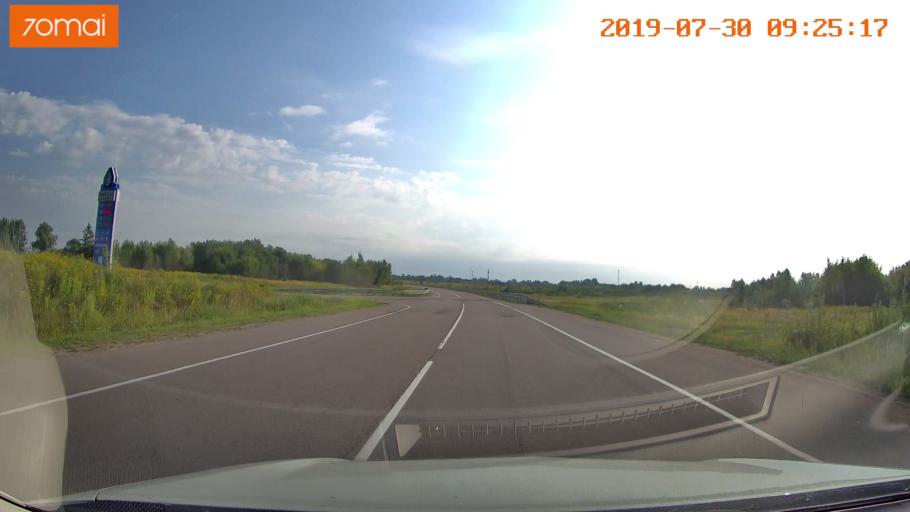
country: LT
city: Kybartai
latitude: 54.6380
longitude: 22.7129
